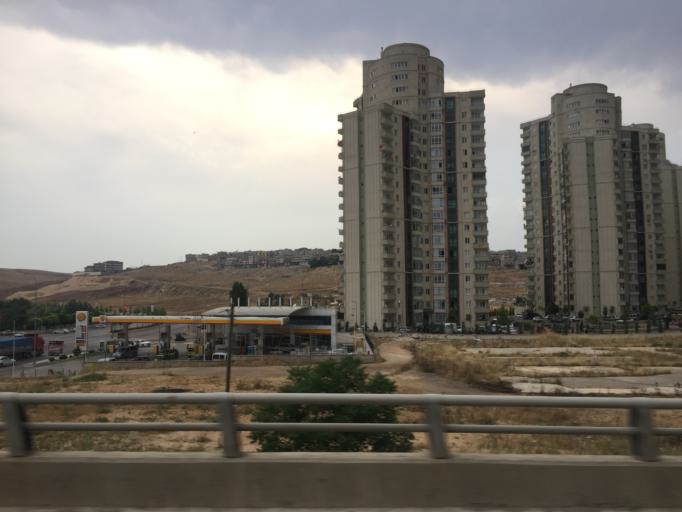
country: TR
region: Gaziantep
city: Gaziantep
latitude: 37.0372
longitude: 37.4235
